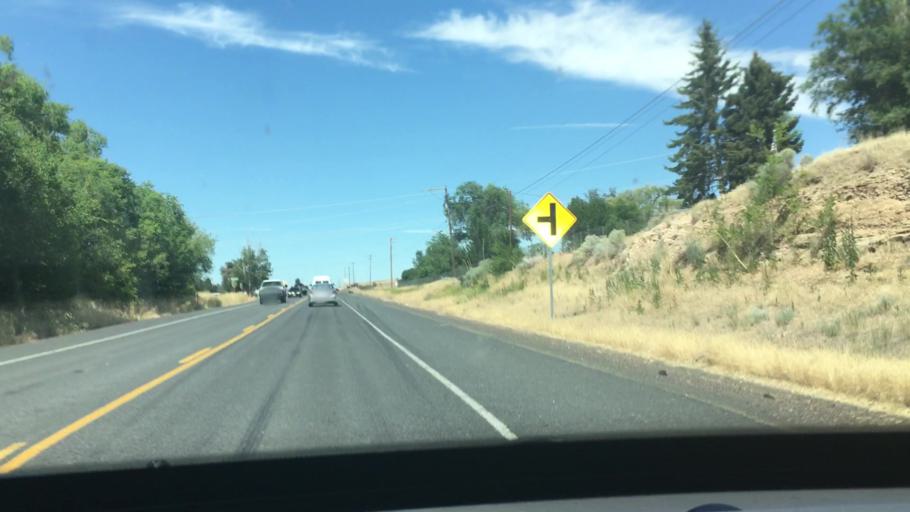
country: US
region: Oregon
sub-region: Jefferson County
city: Culver
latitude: 44.5707
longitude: -121.1601
